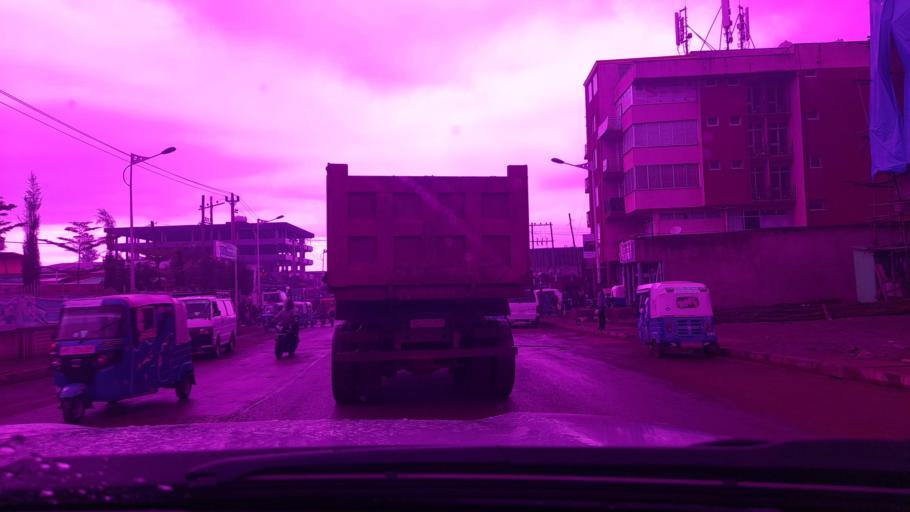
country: ET
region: Oromiya
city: Jima
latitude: 7.6685
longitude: 36.8478
